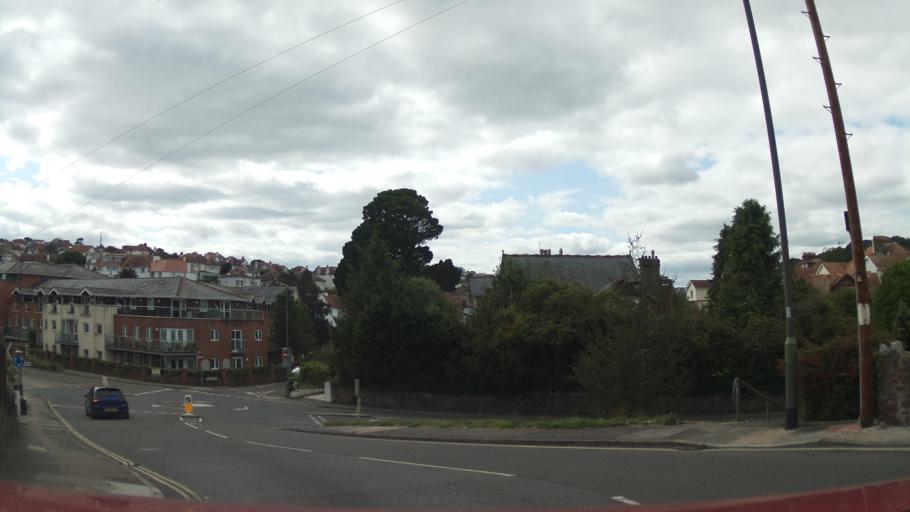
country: GB
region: England
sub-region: Borough of Torbay
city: Paignton
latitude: 50.4307
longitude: -3.5651
